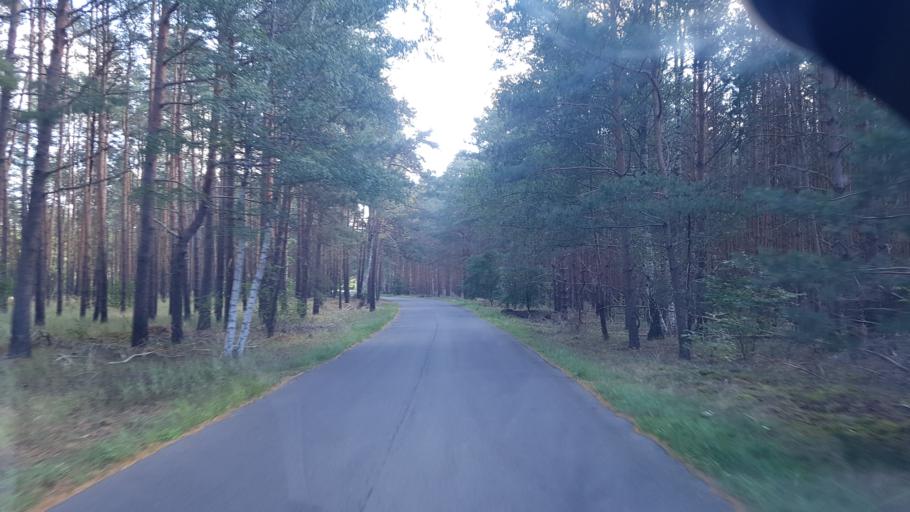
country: DE
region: Brandenburg
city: Drebkau
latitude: 51.6518
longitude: 14.2675
